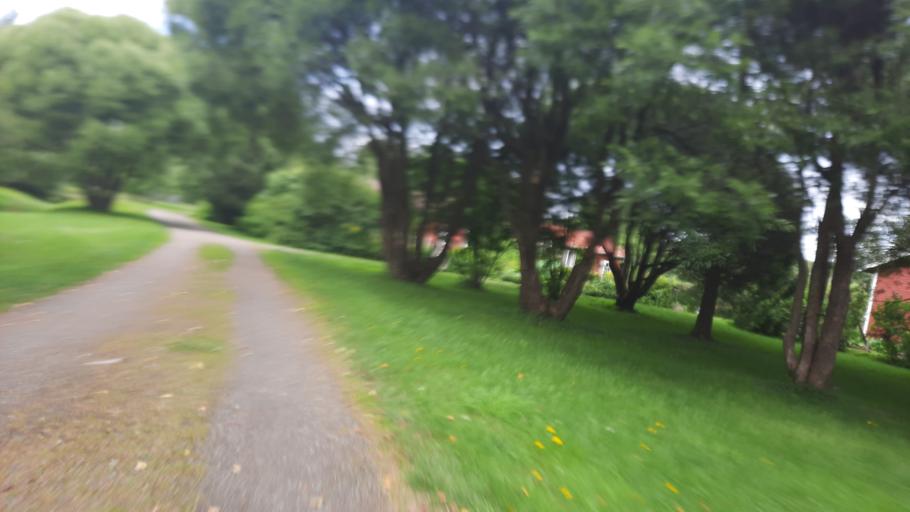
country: FI
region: North Karelia
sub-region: Joensuu
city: Joensuu
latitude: 62.6141
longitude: 29.8489
